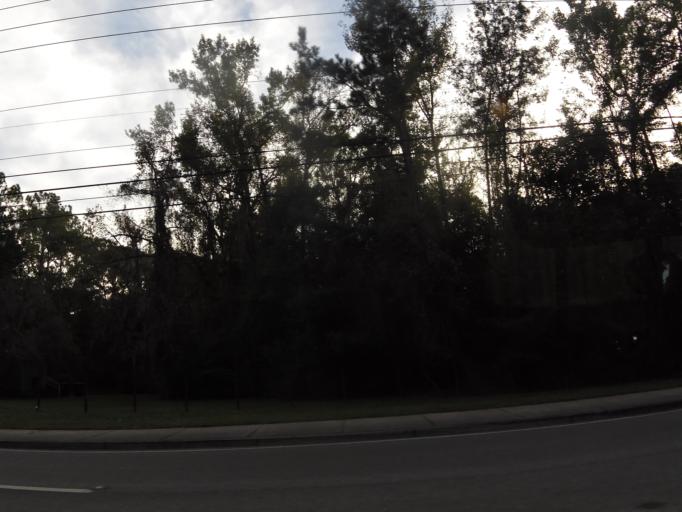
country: US
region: Florida
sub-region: Saint Johns County
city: Fruit Cove
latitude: 30.1603
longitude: -81.6248
